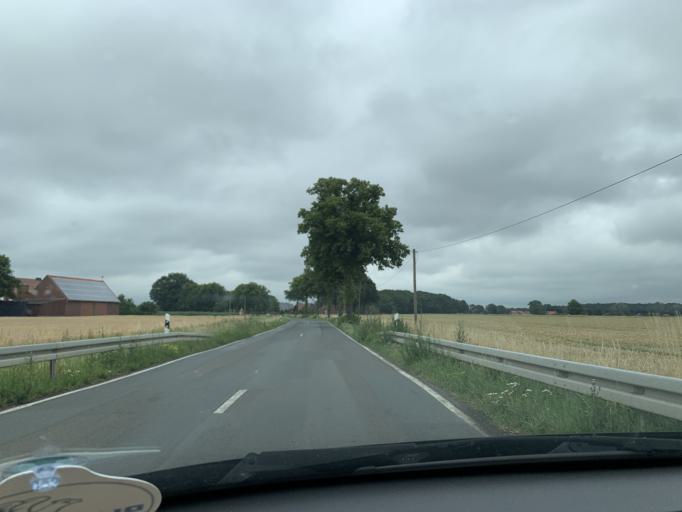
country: DE
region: North Rhine-Westphalia
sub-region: Regierungsbezirk Munster
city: Steinfurt
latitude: 52.1084
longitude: 7.3616
